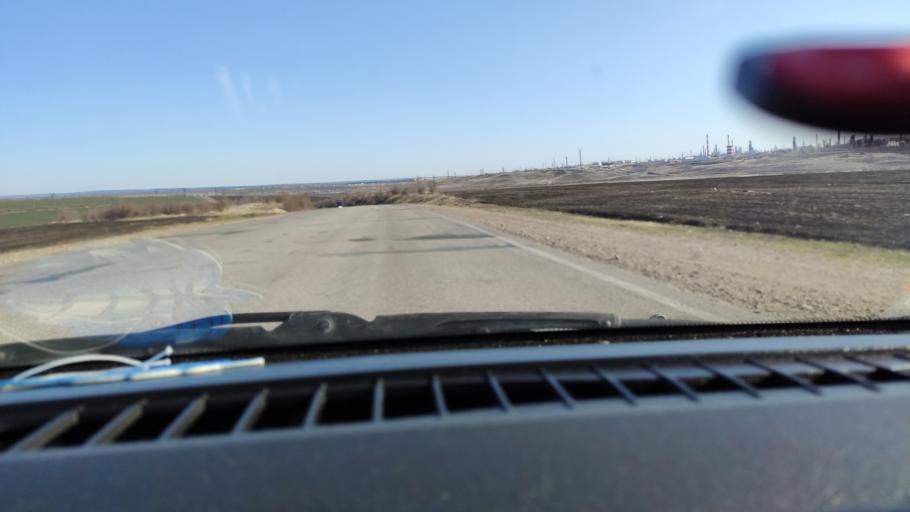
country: RU
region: Samara
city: Varlamovo
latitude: 53.0617
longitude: 48.3517
